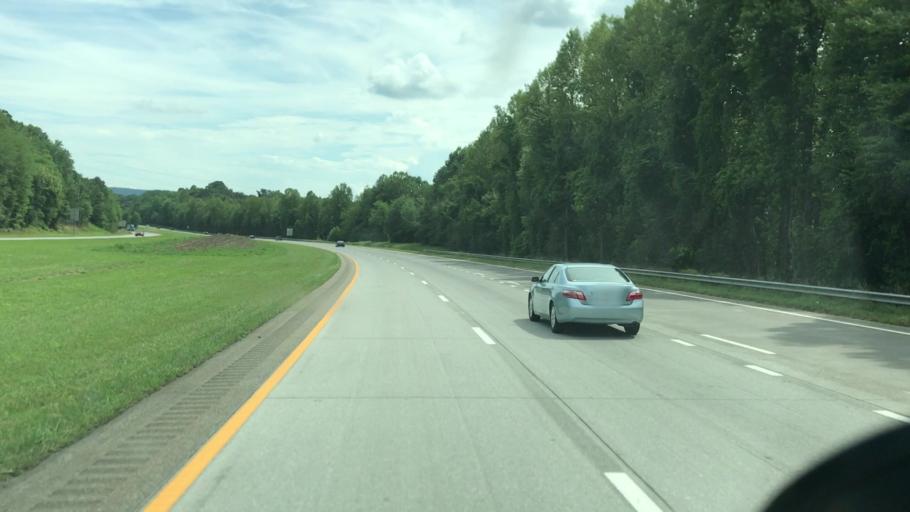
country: US
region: North Carolina
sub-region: Surry County
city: Elkin
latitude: 36.2755
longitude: -80.8246
